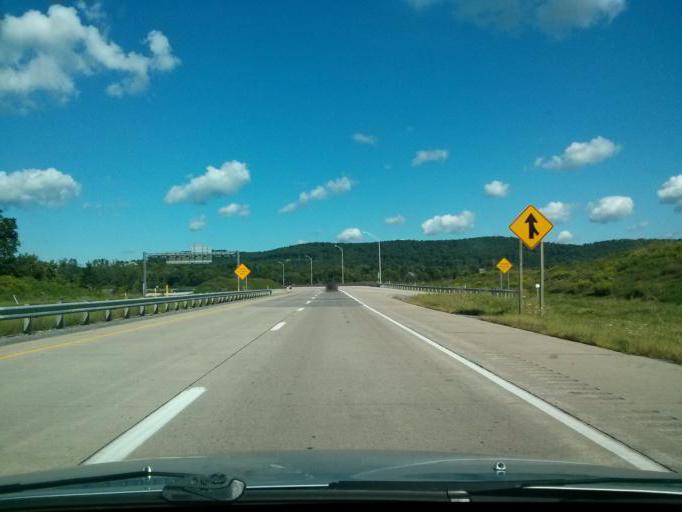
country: US
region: Pennsylvania
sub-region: Centre County
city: Park Forest Village
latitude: 40.8205
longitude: -77.9432
